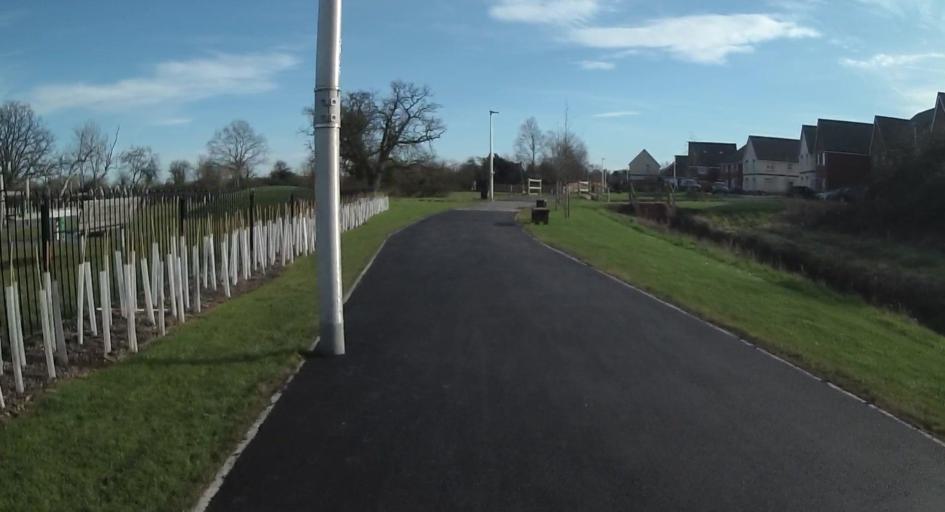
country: GB
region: England
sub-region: Wokingham
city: Shinfield
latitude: 51.4079
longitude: -0.9698
